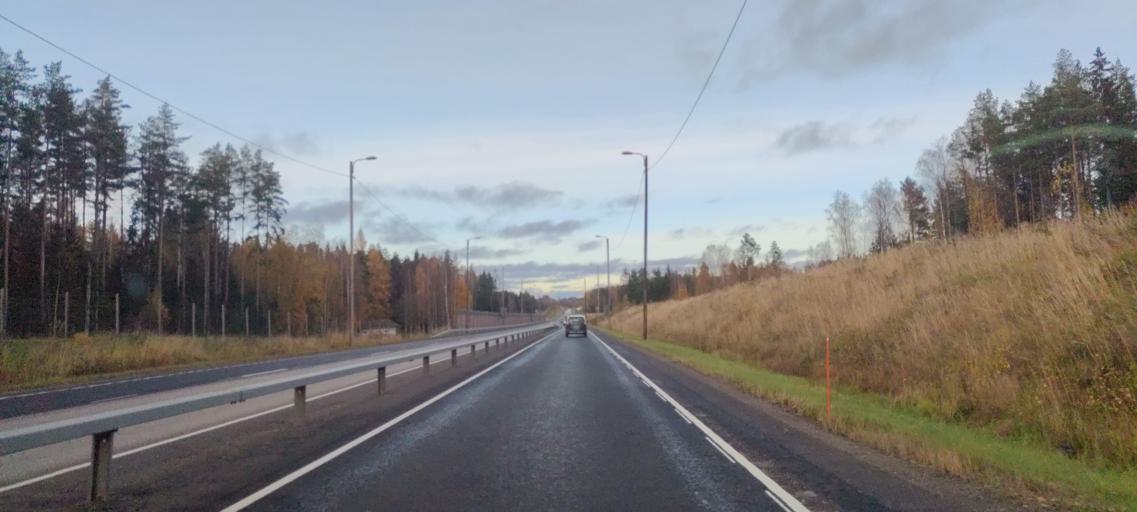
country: FI
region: Satakunta
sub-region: Pori
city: Pori
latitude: 61.4124
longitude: 21.7185
